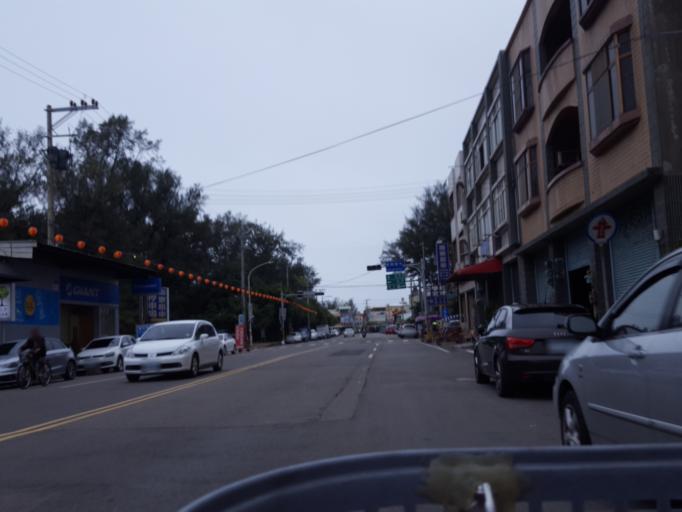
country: TW
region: Taiwan
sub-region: Hsinchu
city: Hsinchu
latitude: 24.8439
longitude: 120.9263
